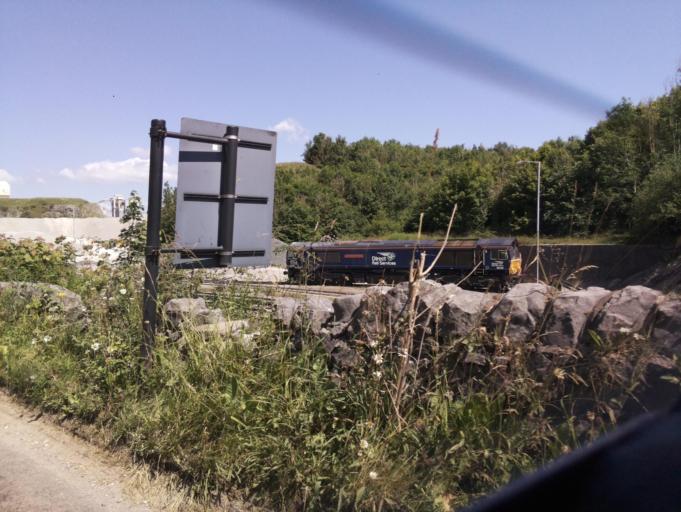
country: GB
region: England
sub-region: Derbyshire
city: Buxton
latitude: 53.2888
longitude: -1.8647
